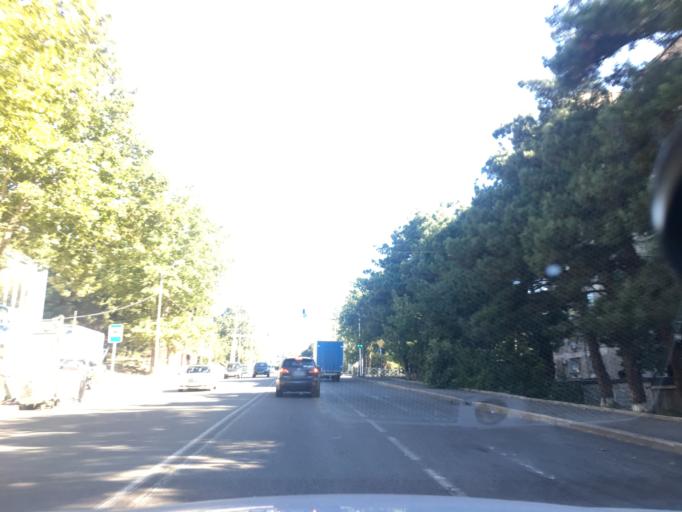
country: GE
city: Zahesi
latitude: 41.7961
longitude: 44.8100
